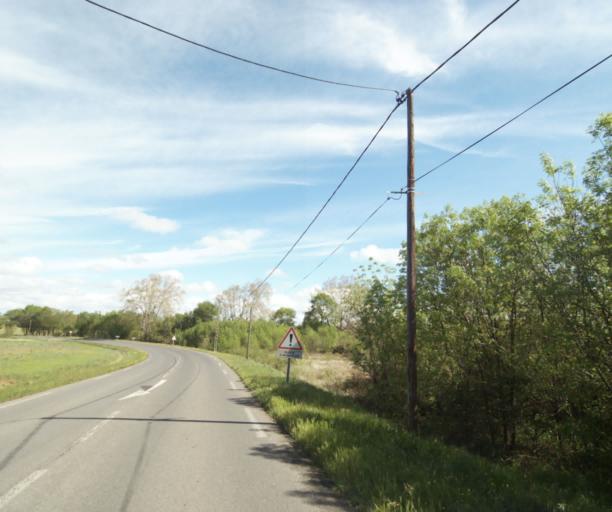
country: FR
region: Languedoc-Roussillon
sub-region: Departement de l'Herault
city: Villeneuve-les-Maguelone
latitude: 43.5444
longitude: 3.8478
